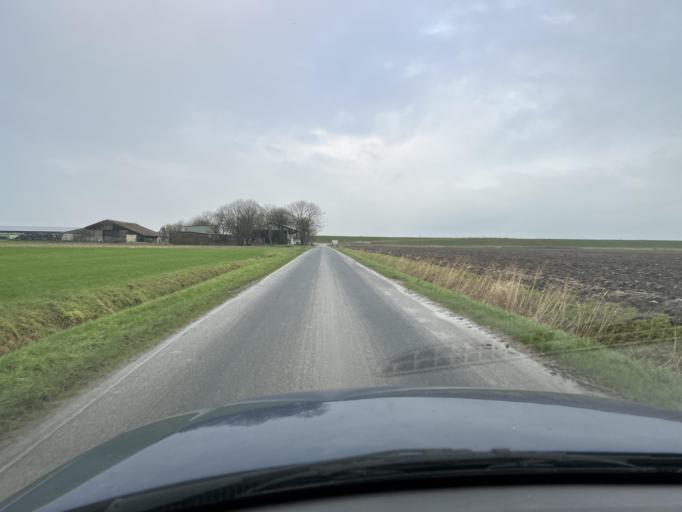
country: DE
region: Schleswig-Holstein
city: Hillgroven
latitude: 54.2204
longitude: 8.8608
